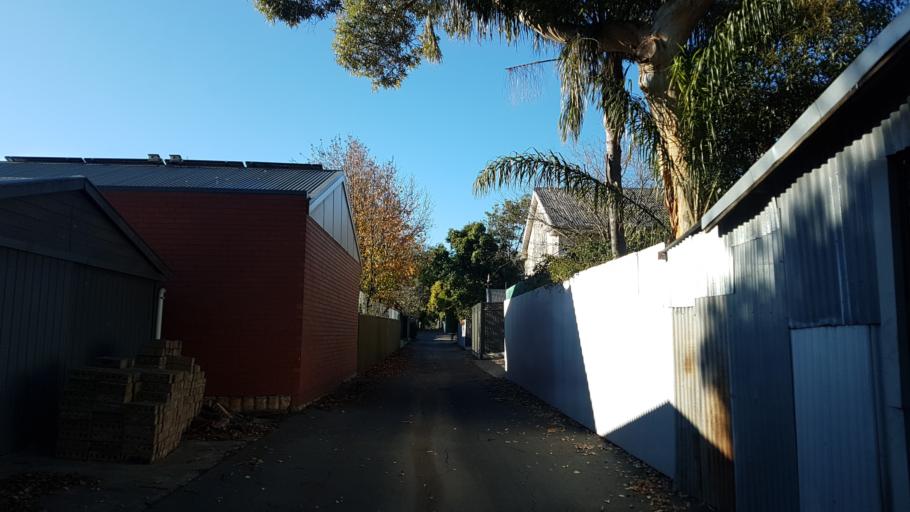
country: AU
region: South Australia
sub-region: Norwood Payneham St Peters
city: Royston Park
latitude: -34.9078
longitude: 138.6237
